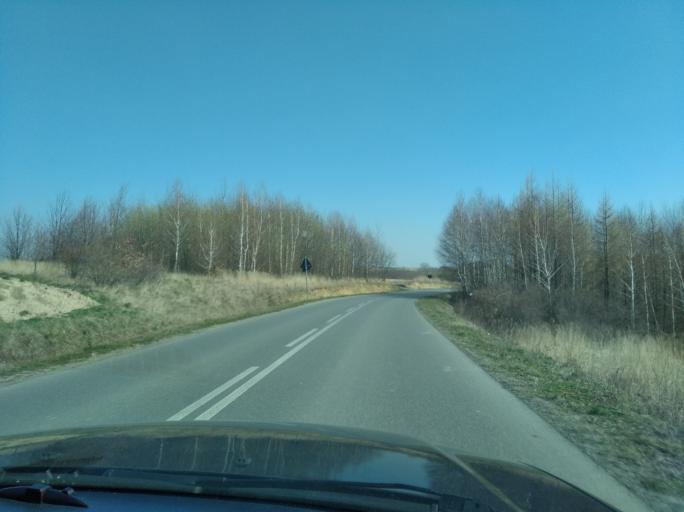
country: PL
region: Subcarpathian Voivodeship
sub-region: Powiat jaroslawski
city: Jodlowka
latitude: 49.8861
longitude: 22.4714
